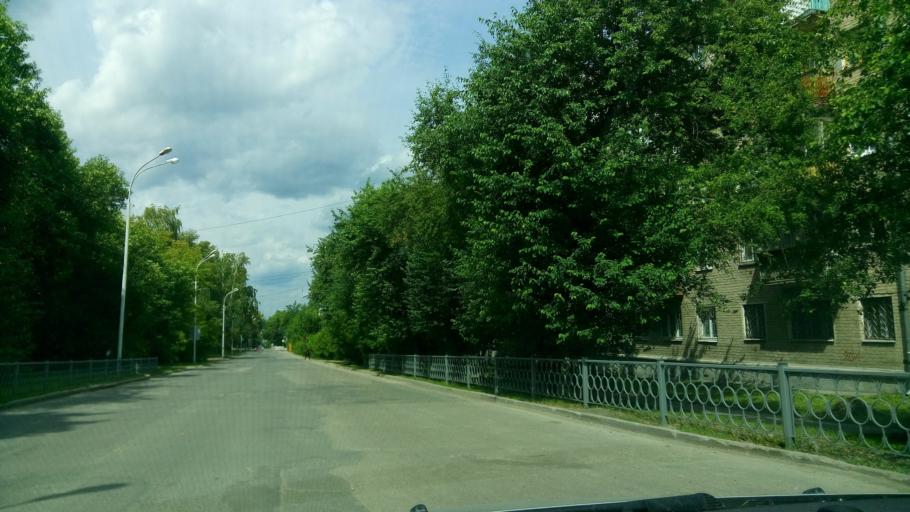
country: RU
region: Sverdlovsk
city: Yekaterinburg
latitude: 56.8873
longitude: 60.6237
